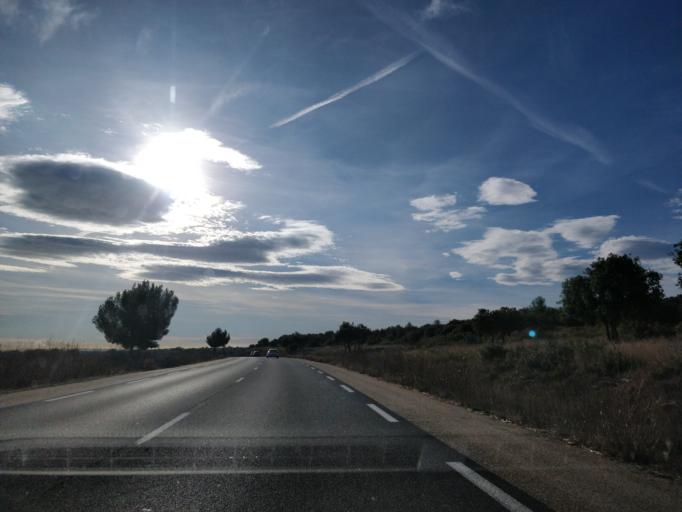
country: FR
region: Languedoc-Roussillon
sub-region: Departement de l'Herault
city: Teyran
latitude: 43.6816
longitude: 3.9459
